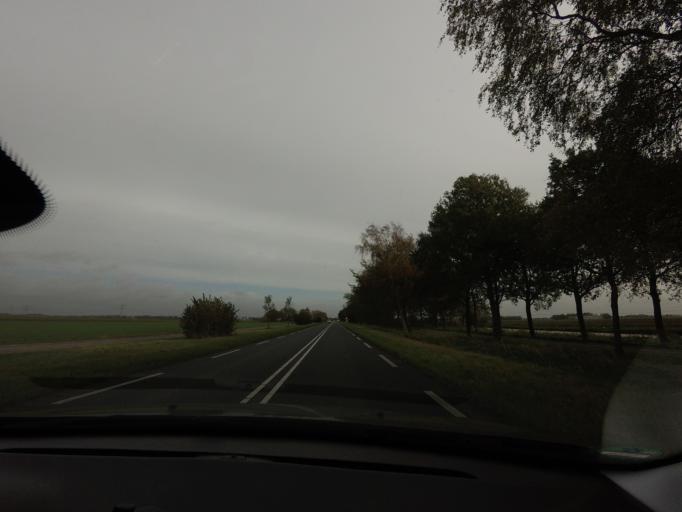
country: NL
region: Flevoland
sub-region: Gemeente Noordoostpolder
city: Emmeloord
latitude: 52.7089
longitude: 5.8105
